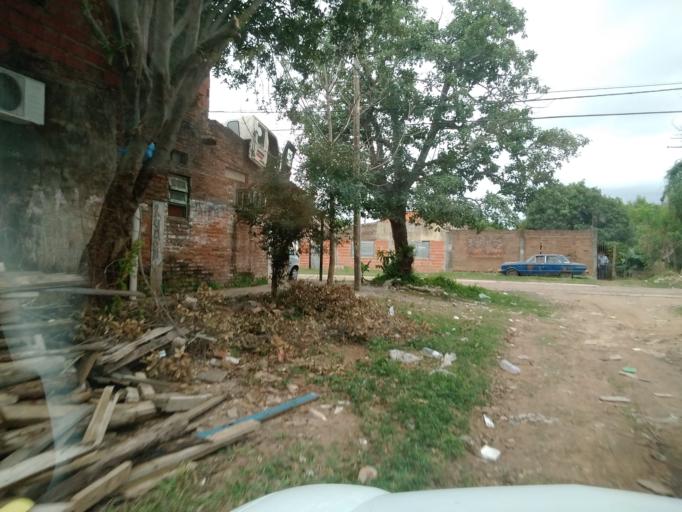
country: AR
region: Corrientes
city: Corrientes
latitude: -27.5069
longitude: -58.7954
